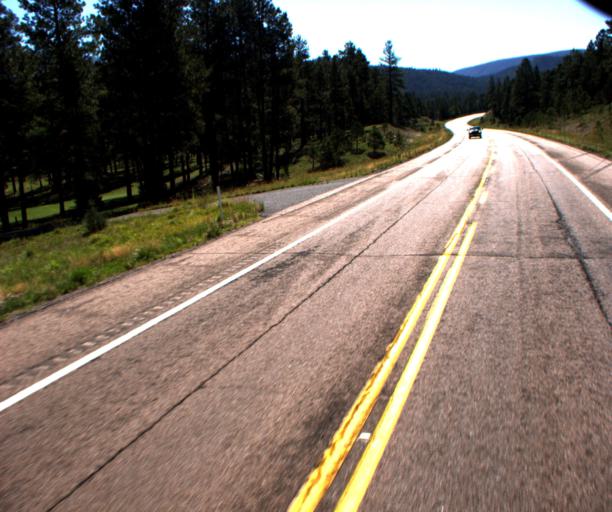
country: US
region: Arizona
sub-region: Apache County
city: Eagar
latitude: 33.9408
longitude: -109.1978
